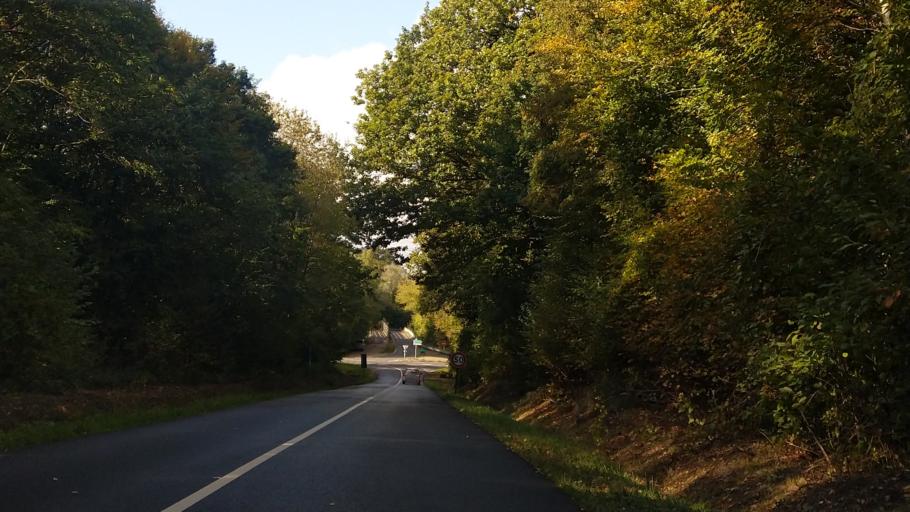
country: FR
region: Ile-de-France
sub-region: Departement du Val-d'Oise
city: L'Isle-Adam
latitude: 49.0829
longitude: 2.2598
